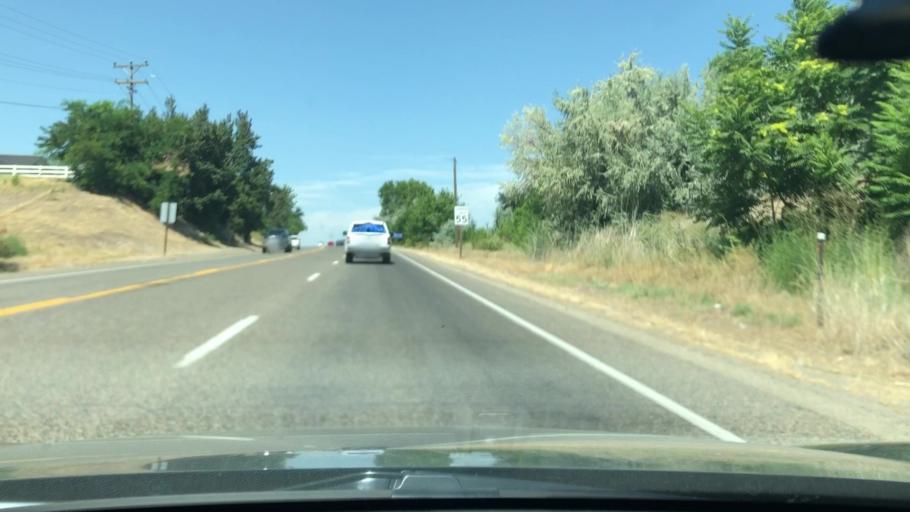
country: US
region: Idaho
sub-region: Canyon County
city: Wilder
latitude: 43.6589
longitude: -116.9117
